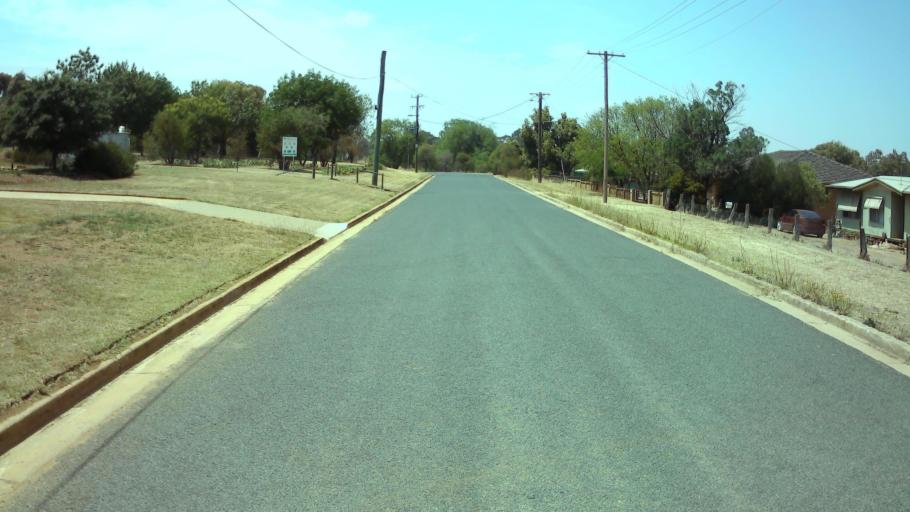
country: AU
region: New South Wales
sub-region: Weddin
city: Grenfell
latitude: -33.8969
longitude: 148.1671
